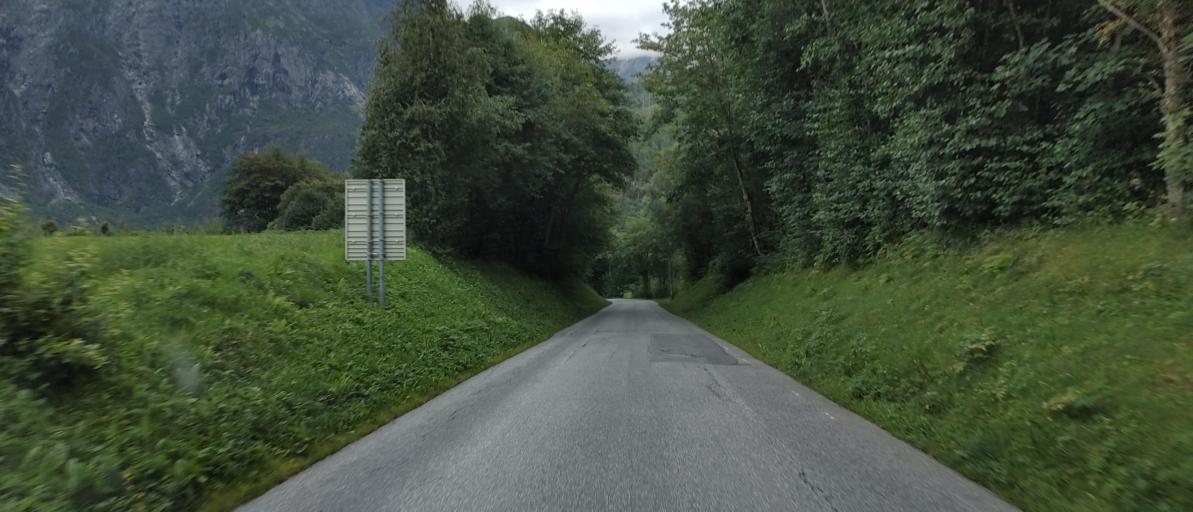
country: NO
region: More og Romsdal
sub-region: Rauma
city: Andalsnes
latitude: 62.5268
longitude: 7.7136
